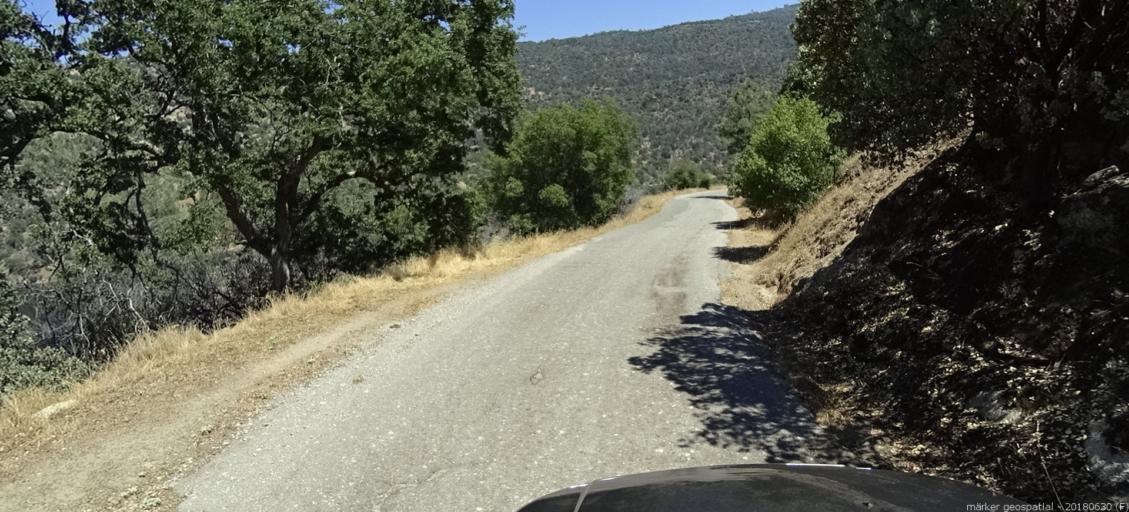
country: US
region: California
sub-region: Fresno County
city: Auberry
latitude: 37.1548
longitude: -119.4373
